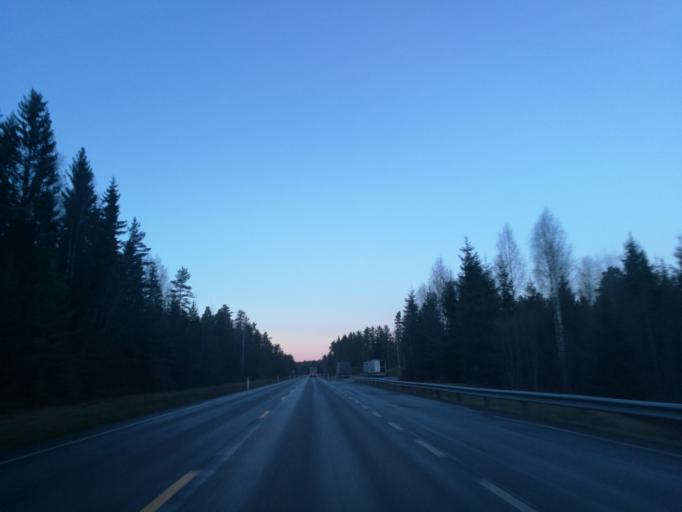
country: NO
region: Hedmark
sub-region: Eidskog
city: Skotterud
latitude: 60.0025
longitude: 12.1084
